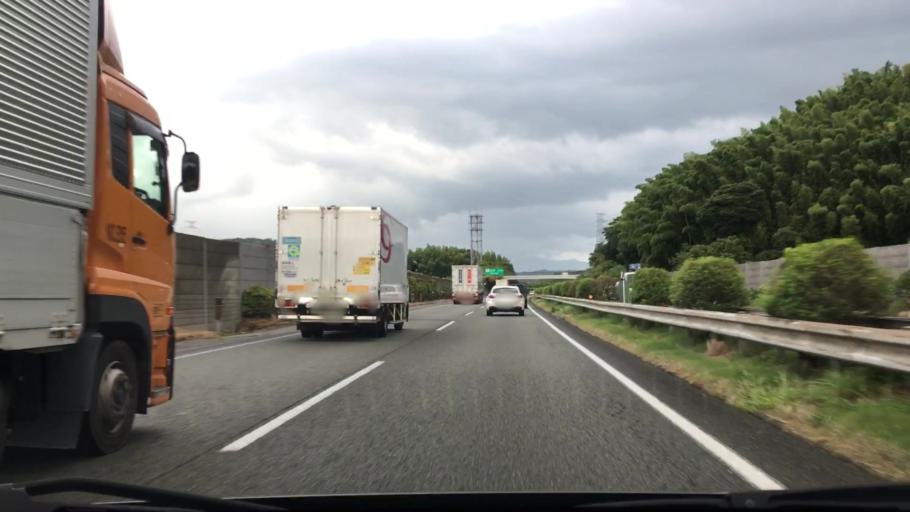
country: JP
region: Fukuoka
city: Miyata
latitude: 33.7505
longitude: 130.5833
